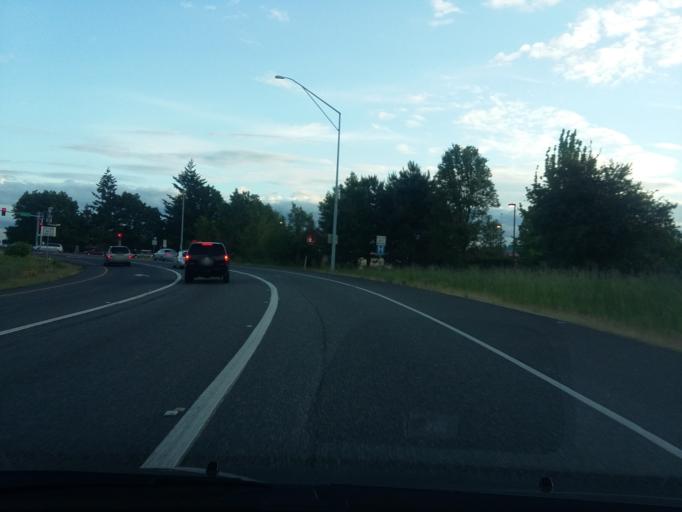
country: US
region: Washington
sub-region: Clark County
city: Orchards
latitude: 45.6221
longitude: -122.5615
